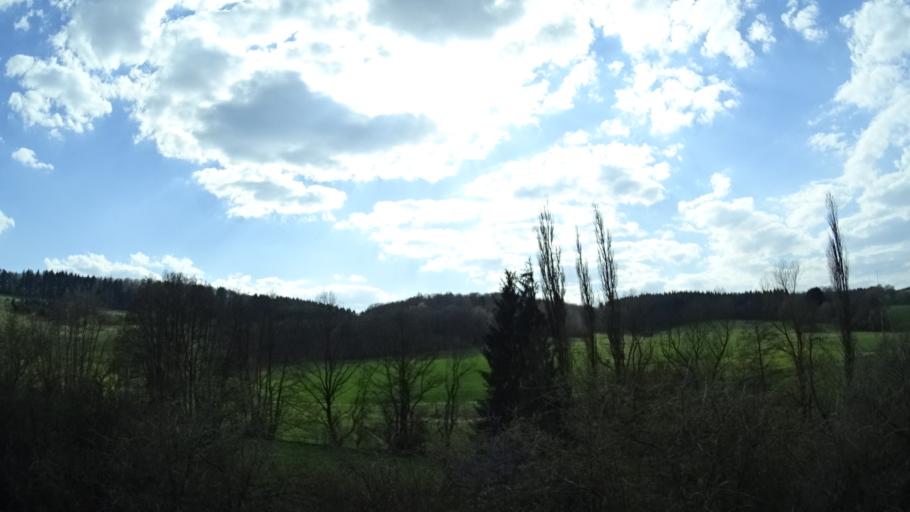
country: DE
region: Rheinland-Pfalz
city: Barenbach
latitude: 49.7420
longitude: 7.4488
